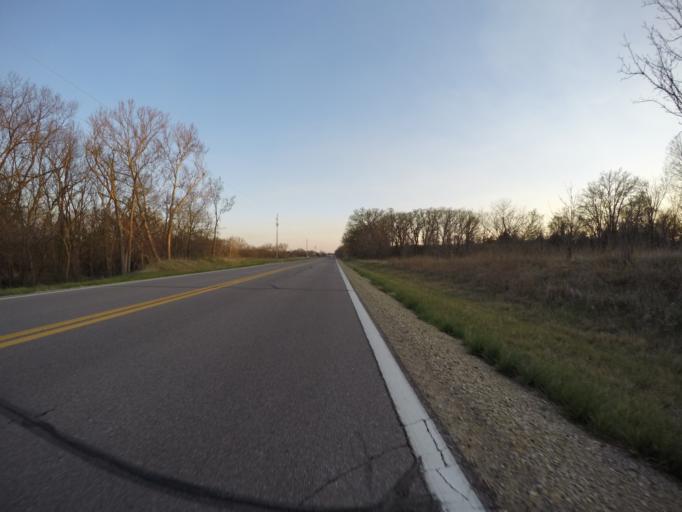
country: US
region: Kansas
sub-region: Riley County
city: Ogden
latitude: 39.0832
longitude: -96.6556
